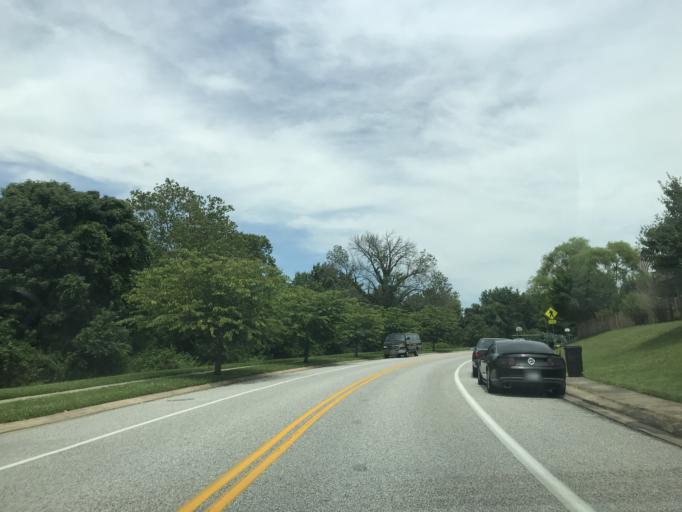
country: US
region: Maryland
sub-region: Harford County
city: South Bel Air
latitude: 39.5528
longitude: -76.3282
